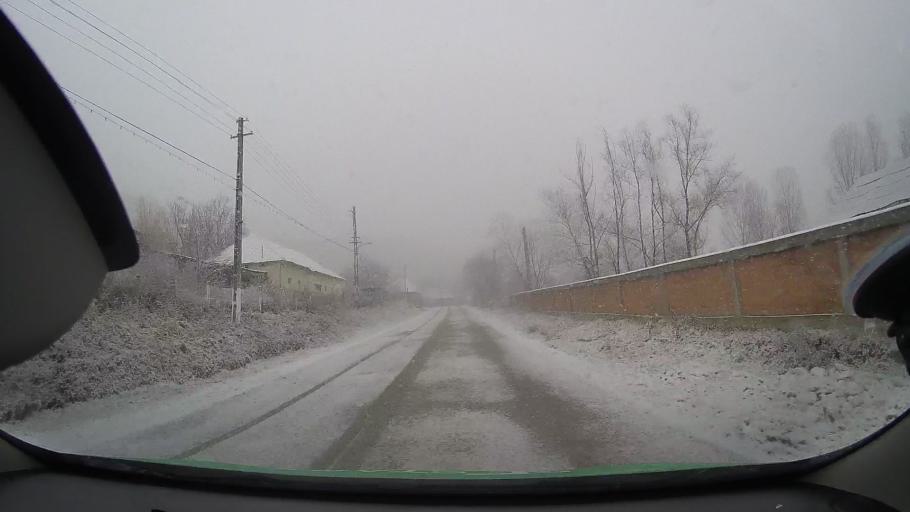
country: RO
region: Alba
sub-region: Comuna Hoparta
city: Hoparta
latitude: 46.3159
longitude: 23.8617
